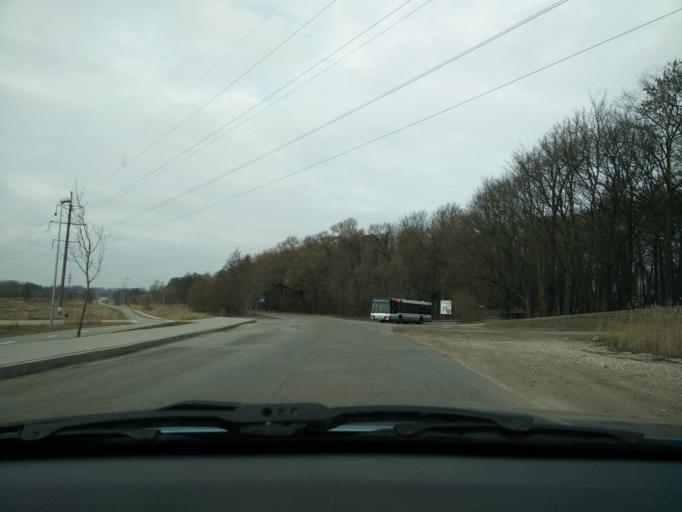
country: LT
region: Klaipedos apskritis
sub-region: Klaipeda
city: Klaipeda
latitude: 55.7214
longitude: 21.1699
